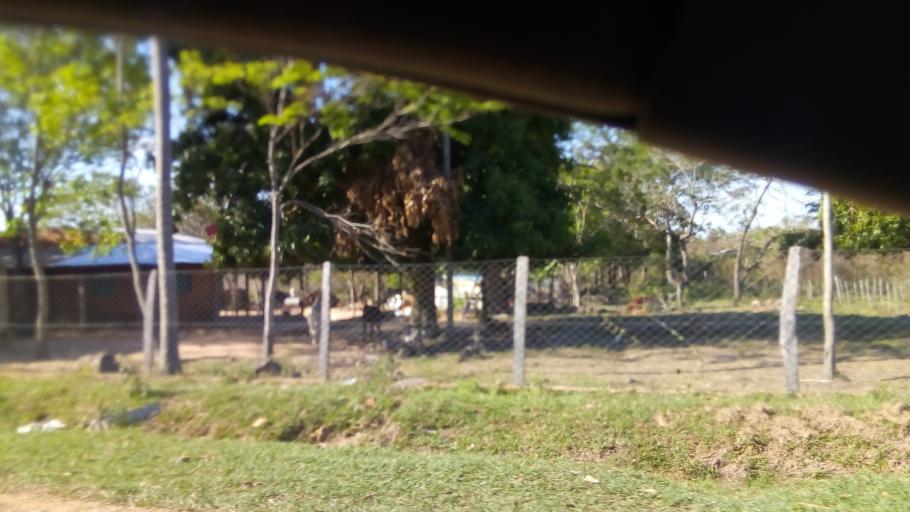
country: PY
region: Cordillera
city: Arroyos y Esteros
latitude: -24.9957
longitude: -57.1863
